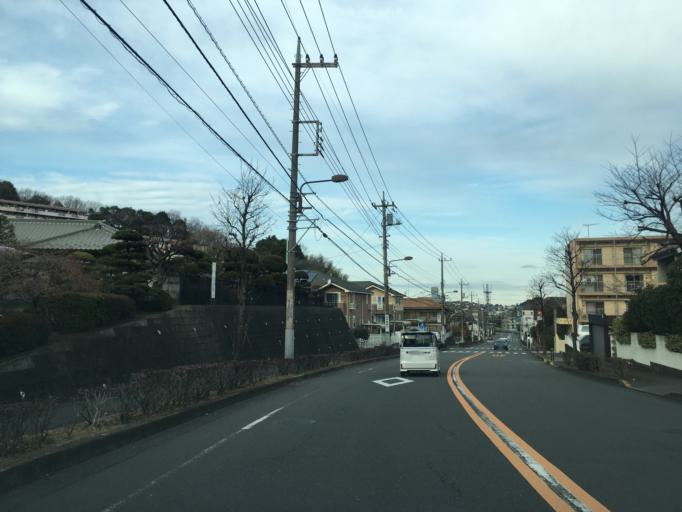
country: JP
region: Tokyo
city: Hino
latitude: 35.6253
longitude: 139.4372
